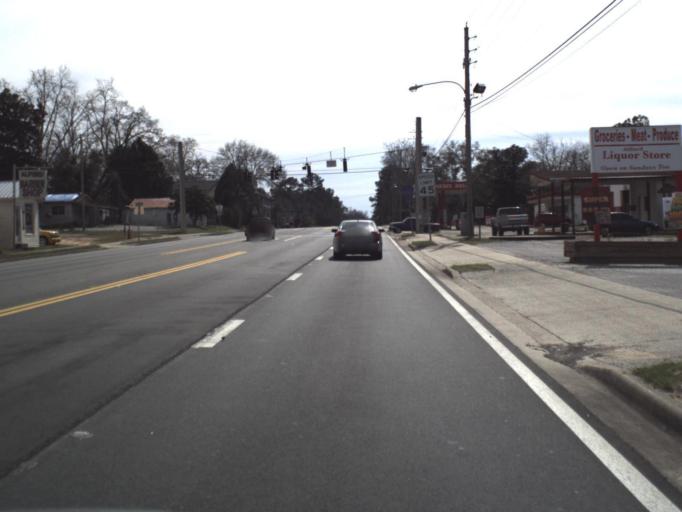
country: US
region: Florida
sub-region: Washington County
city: Chipley
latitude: 30.6949
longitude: -85.3921
